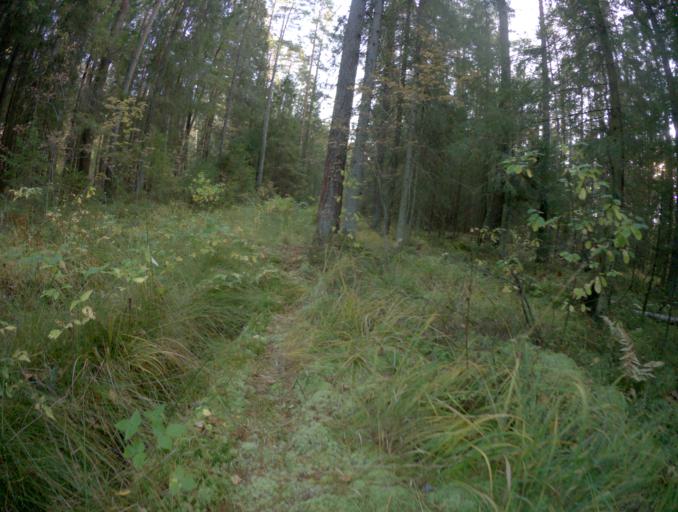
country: RU
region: Vladimir
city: Raduzhnyy
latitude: 56.0198
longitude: 40.2585
